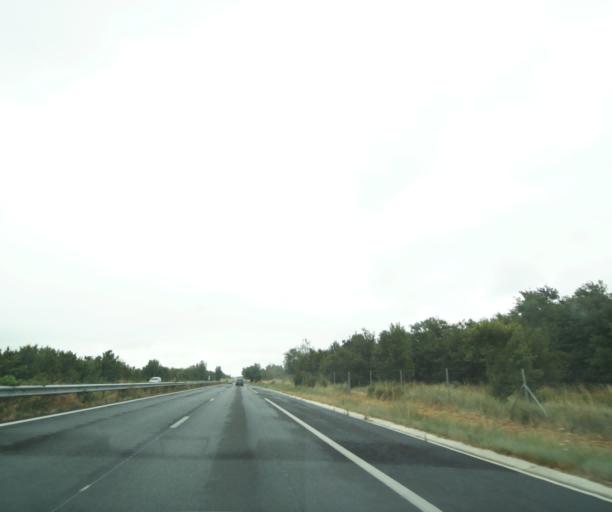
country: FR
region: Midi-Pyrenees
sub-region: Departement du Tarn
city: Lisle-sur-Tarn
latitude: 43.8307
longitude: 1.8279
